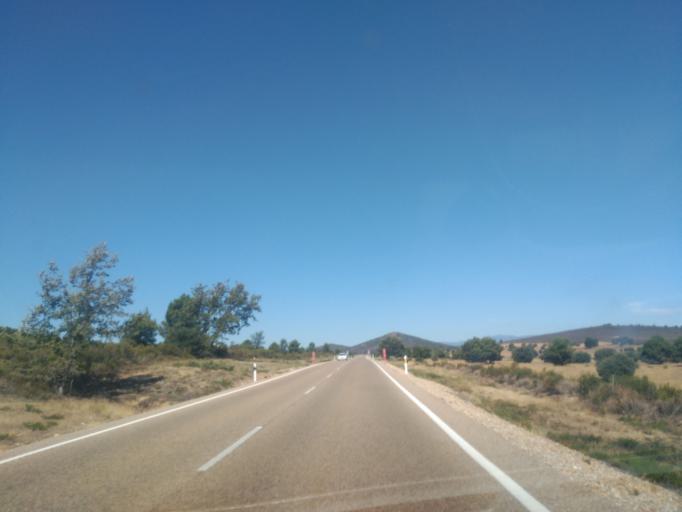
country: ES
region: Castille and Leon
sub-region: Provincia de Zamora
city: Otero de Bodas
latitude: 41.9303
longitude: -6.1150
